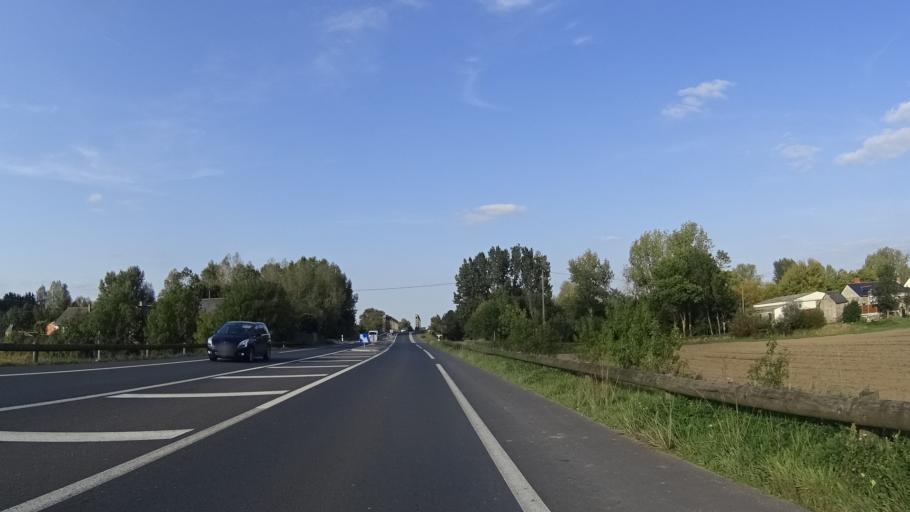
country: FR
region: Pays de la Loire
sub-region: Departement de Maine-et-Loire
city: Chalonnes-sur-Loire
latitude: 47.3618
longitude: -0.7577
